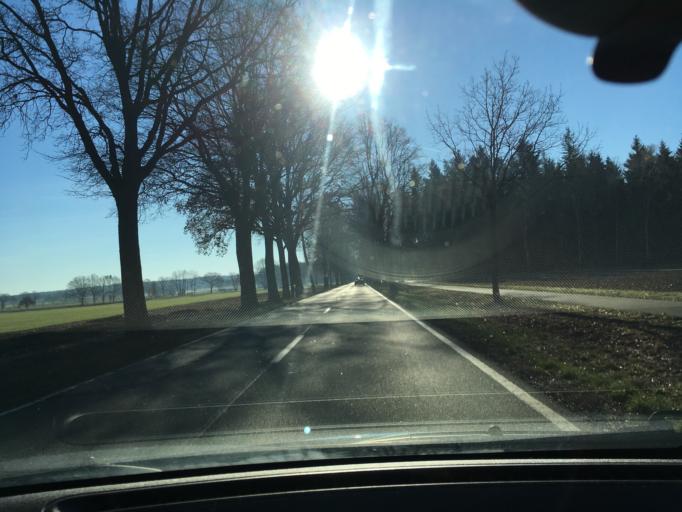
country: DE
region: Lower Saxony
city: Ebstorf
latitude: 53.0479
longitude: 10.4121
